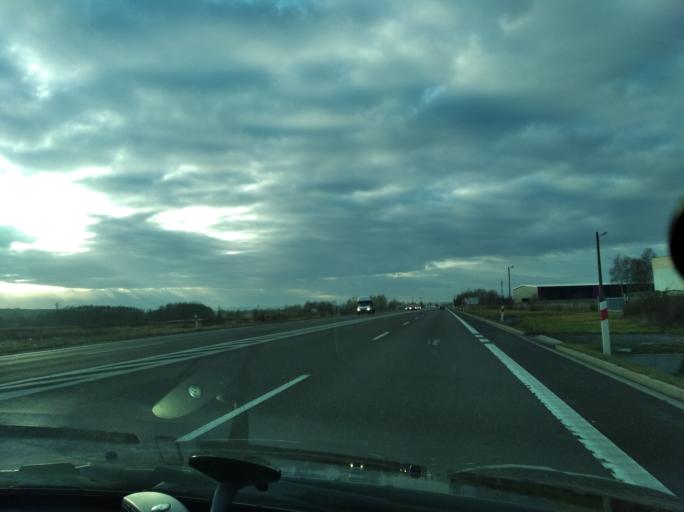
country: PL
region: Subcarpathian Voivodeship
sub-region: Powiat rzeszowski
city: Krasne
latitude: 50.0427
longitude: 22.1125
